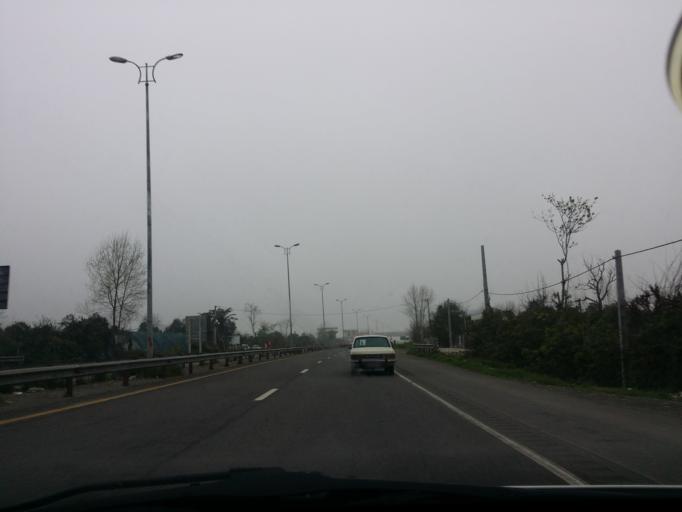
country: IR
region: Mazandaran
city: Tonekabon
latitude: 36.8195
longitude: 50.8485
